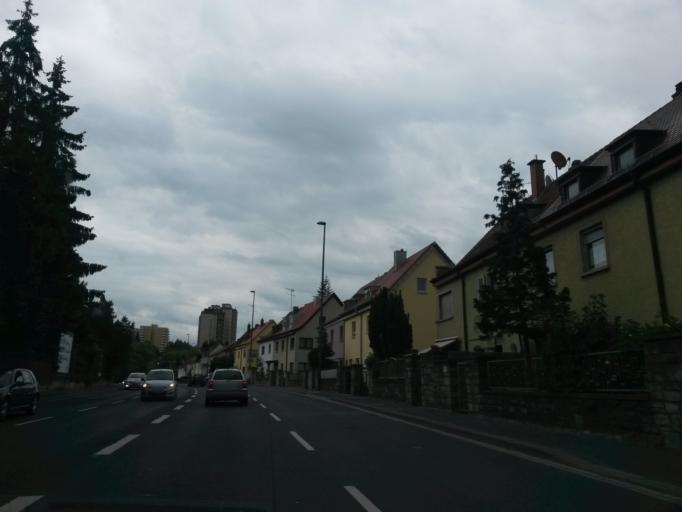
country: DE
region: Bavaria
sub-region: Regierungsbezirk Unterfranken
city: Wuerzburg
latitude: 49.8053
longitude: 9.9616
